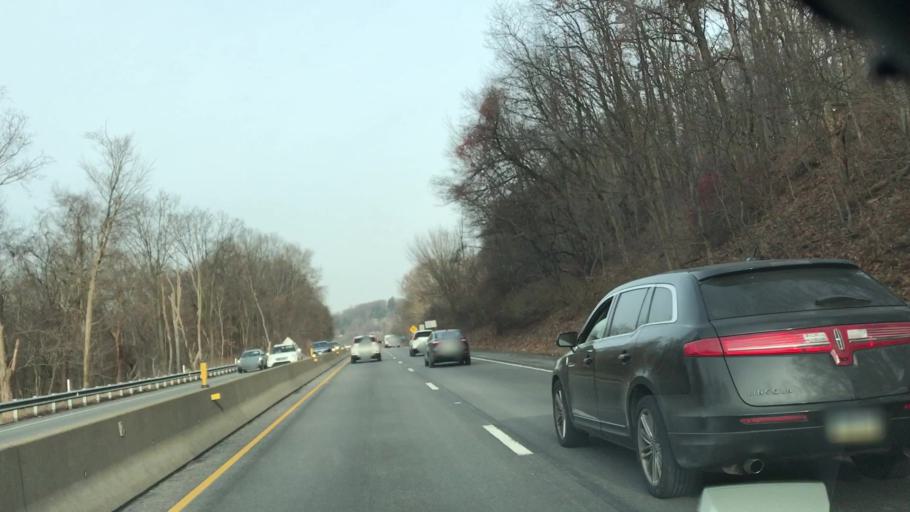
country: US
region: Pennsylvania
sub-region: Allegheny County
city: West View
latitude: 40.5784
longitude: -80.0268
